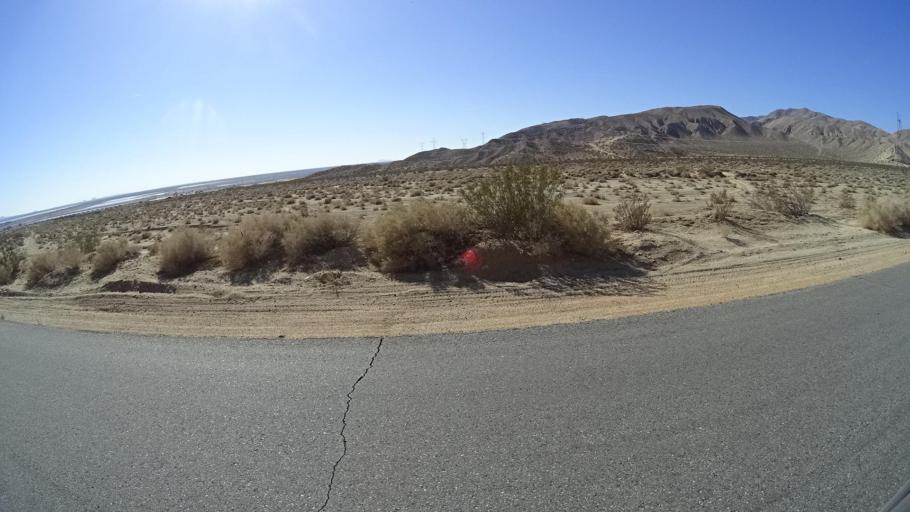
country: US
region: California
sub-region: Kern County
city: California City
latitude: 35.3034
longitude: -118.0053
